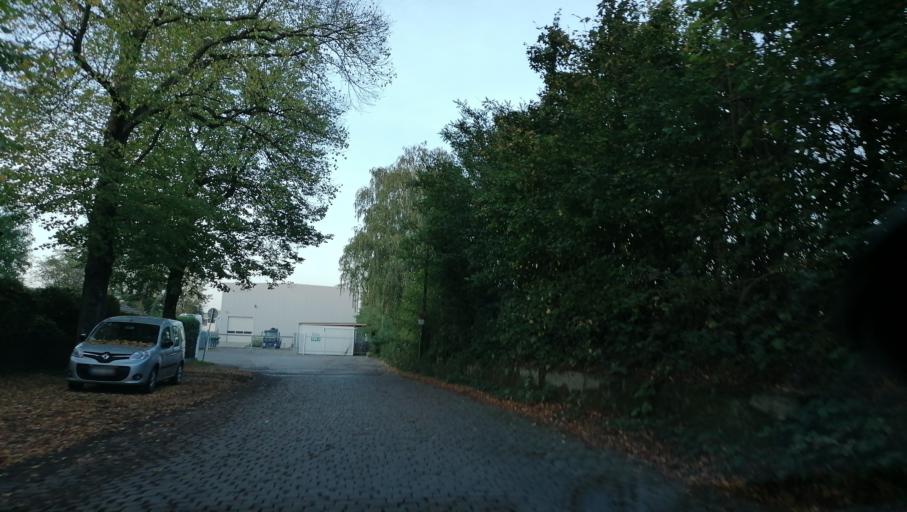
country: DE
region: North Rhine-Westphalia
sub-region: Regierungsbezirk Arnsberg
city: Herne
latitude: 51.5631
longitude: 7.1956
